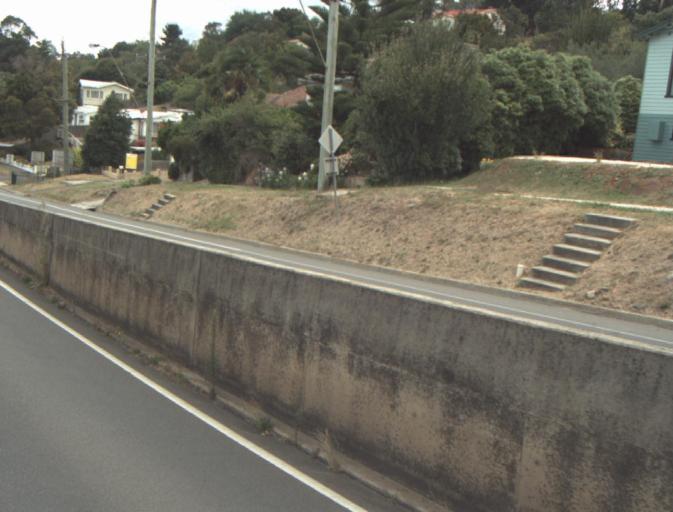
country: AU
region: Tasmania
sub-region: Launceston
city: Launceston
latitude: -41.4262
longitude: 147.1169
